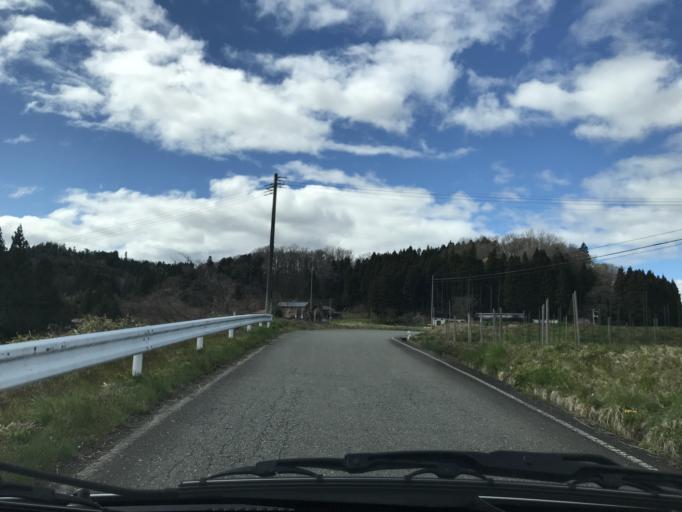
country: JP
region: Iwate
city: Mizusawa
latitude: 39.0353
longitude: 141.0560
